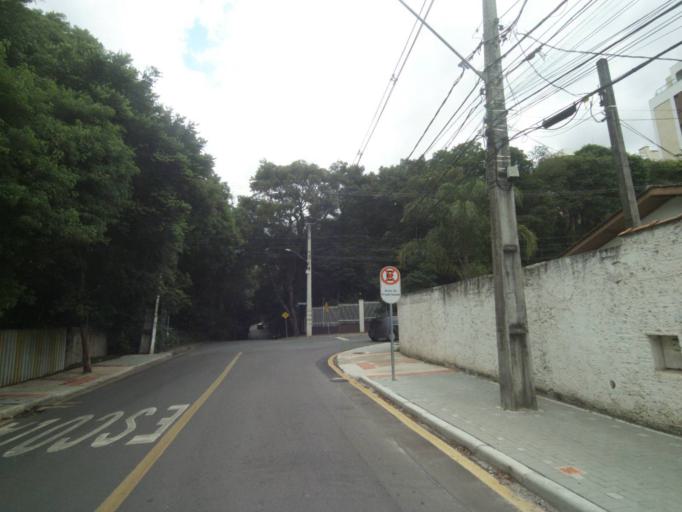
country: BR
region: Parana
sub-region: Curitiba
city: Curitiba
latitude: -25.4350
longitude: -49.3252
